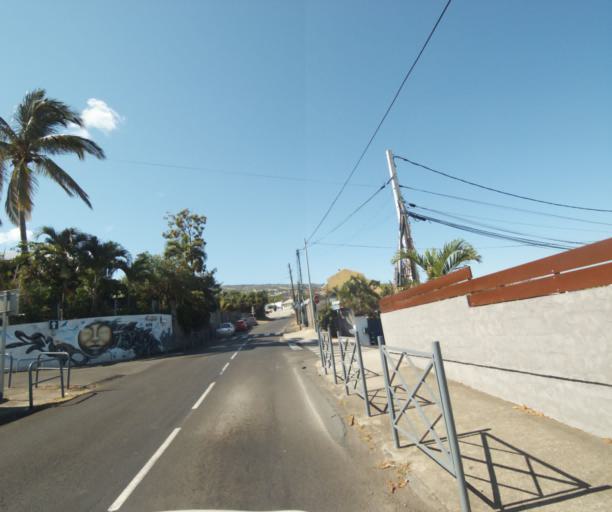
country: RE
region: Reunion
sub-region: Reunion
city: La Possession
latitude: -20.9804
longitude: 55.3241
